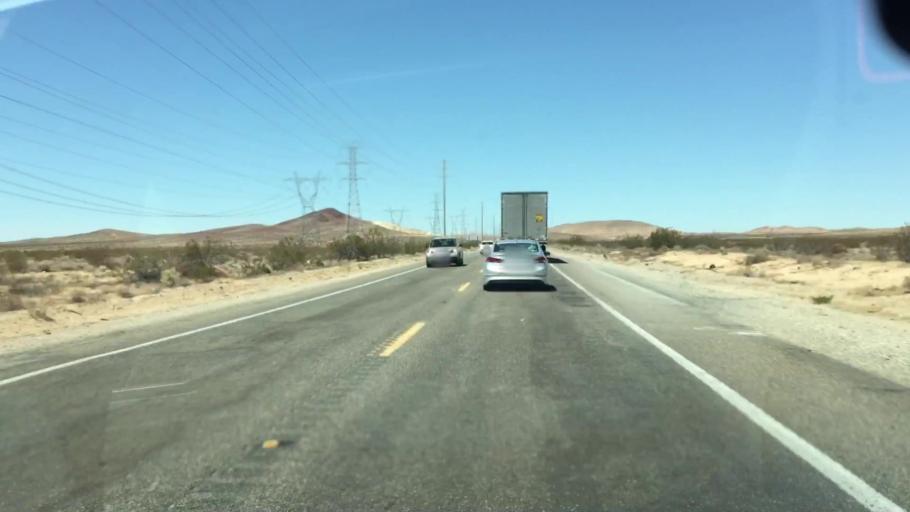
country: US
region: California
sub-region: Kern County
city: Boron
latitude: 34.8486
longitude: -117.5017
